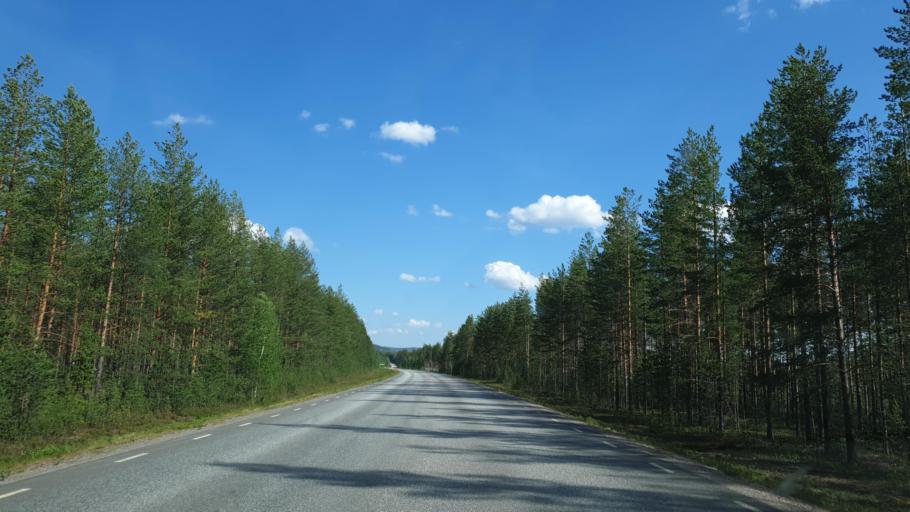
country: SE
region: Norrbotten
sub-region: Alvsbyns Kommun
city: AElvsbyn
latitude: 65.8118
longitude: 20.5931
